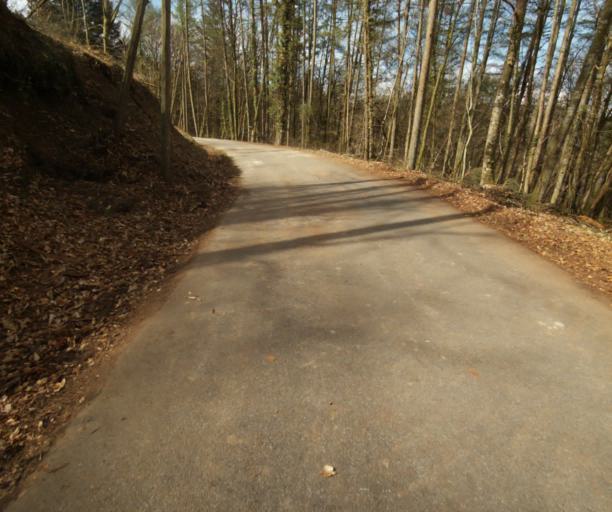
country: FR
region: Limousin
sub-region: Departement de la Correze
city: Correze
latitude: 45.3602
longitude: 1.8688
